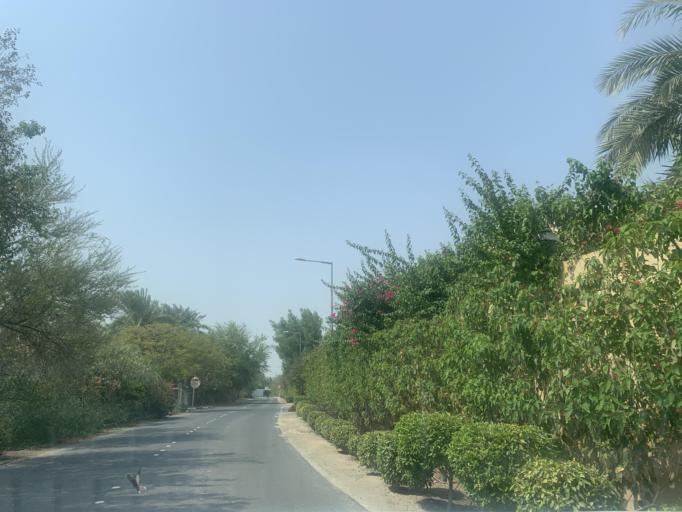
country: BH
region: Central Governorate
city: Madinat Hamad
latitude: 26.1678
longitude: 50.4534
